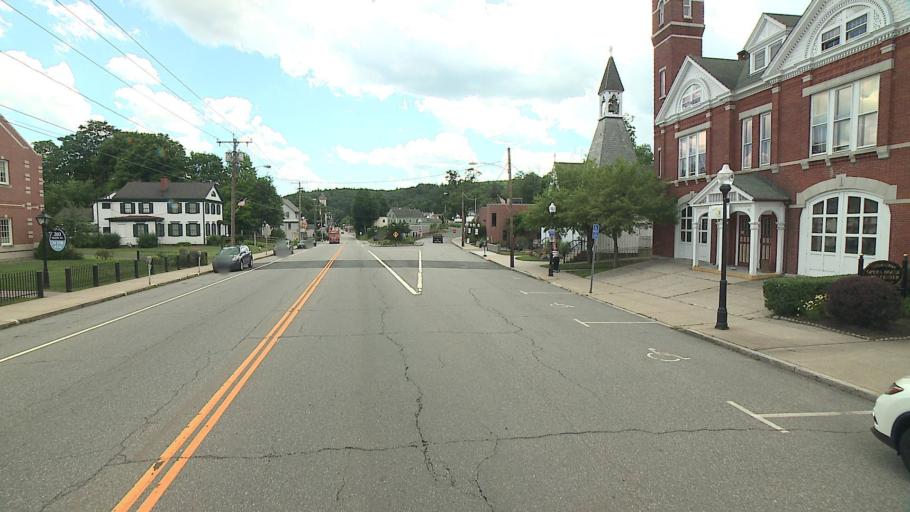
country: US
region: Connecticut
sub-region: Litchfield County
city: Thomaston
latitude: 41.6727
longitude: -73.0750
